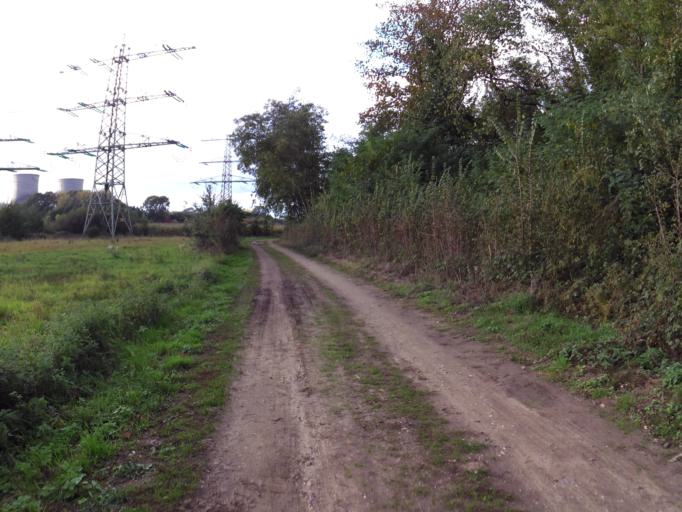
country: NL
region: Limburg
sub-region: Gemeente Maasgouw
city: Maasbracht
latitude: 51.1526
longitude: 5.9213
